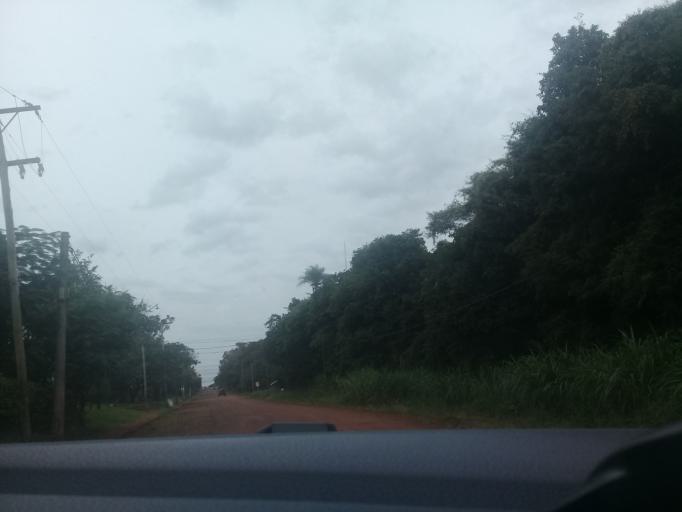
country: AR
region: Misiones
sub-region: Departamento de Obera
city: Obera
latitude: -27.4806
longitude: -55.1532
